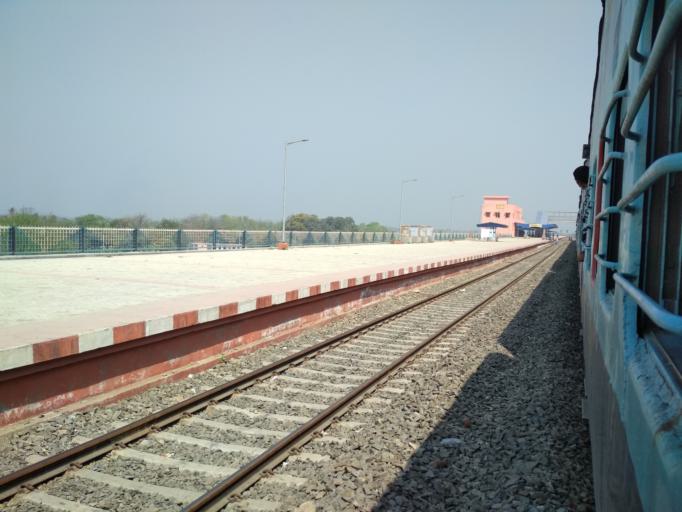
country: IN
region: Bihar
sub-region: Munger
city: Munger
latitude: 25.4260
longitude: 86.4386
